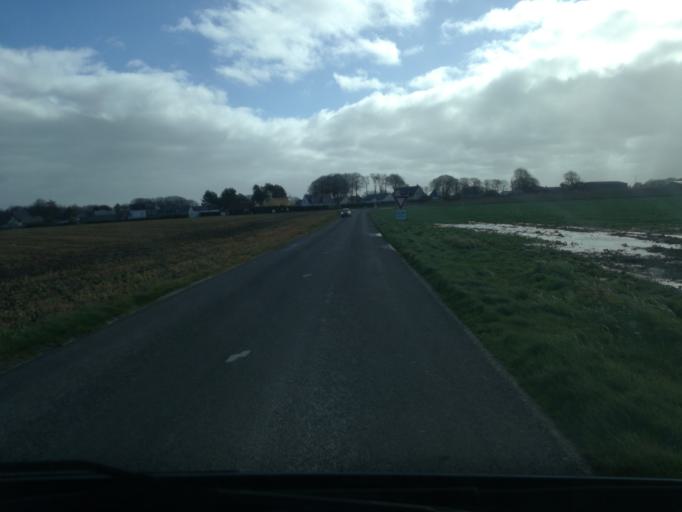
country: FR
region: Haute-Normandie
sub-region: Departement de la Seine-Maritime
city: Saint-Leonard
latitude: 49.7370
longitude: 0.3463
